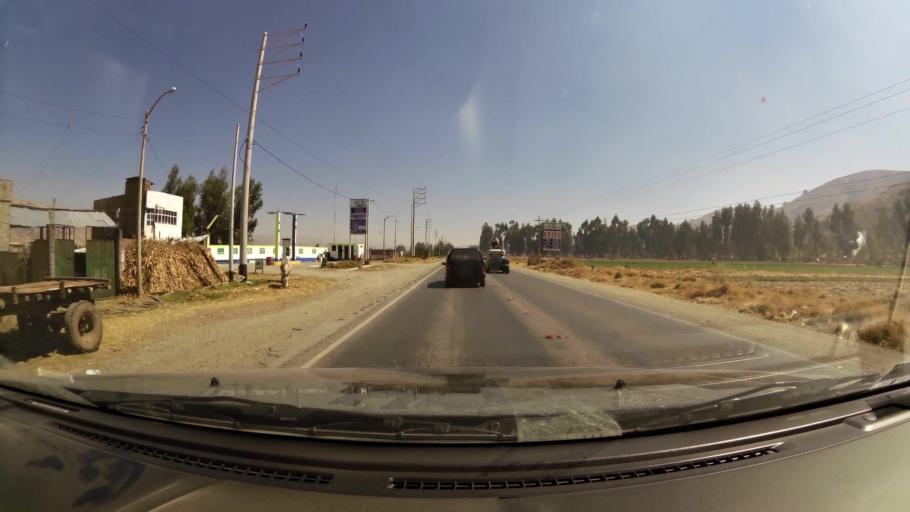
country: PE
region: Junin
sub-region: Provincia de Jauja
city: Huamali
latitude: -11.8267
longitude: -75.4067
